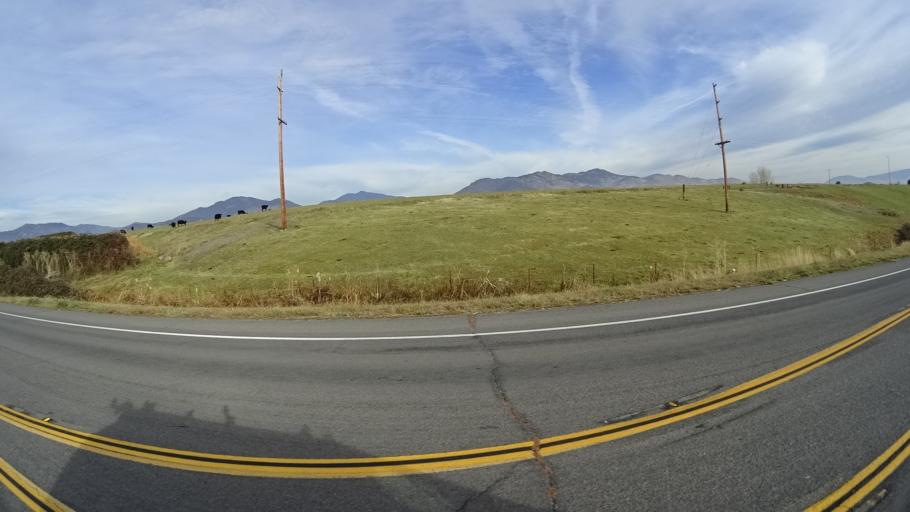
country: US
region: California
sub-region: Siskiyou County
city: Montague
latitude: 41.7288
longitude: -122.5688
